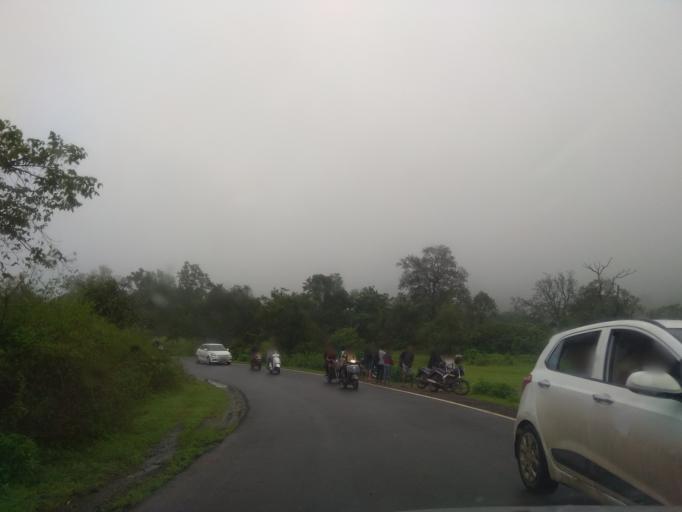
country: IN
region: Maharashtra
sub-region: Raigarh
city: Indapur
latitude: 18.4905
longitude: 73.4256
